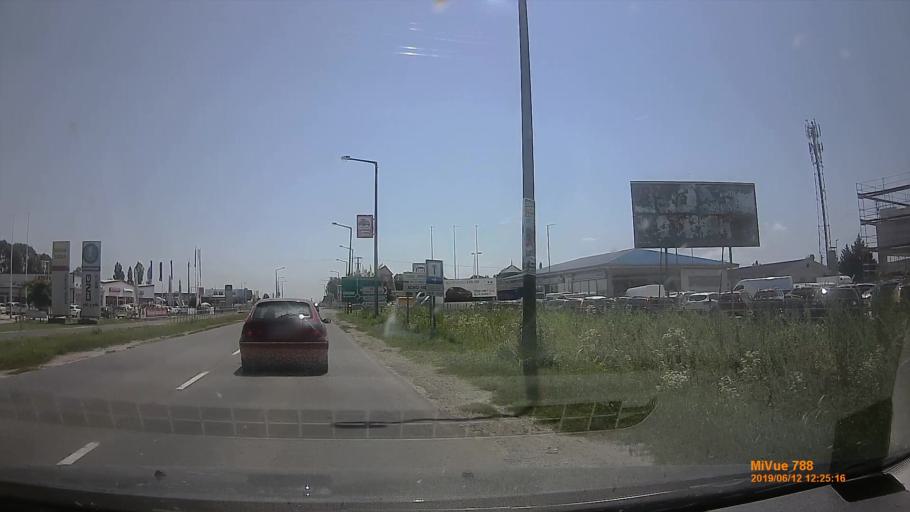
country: HU
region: Bacs-Kiskun
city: Kecskemet
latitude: 46.8832
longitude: 19.7061
